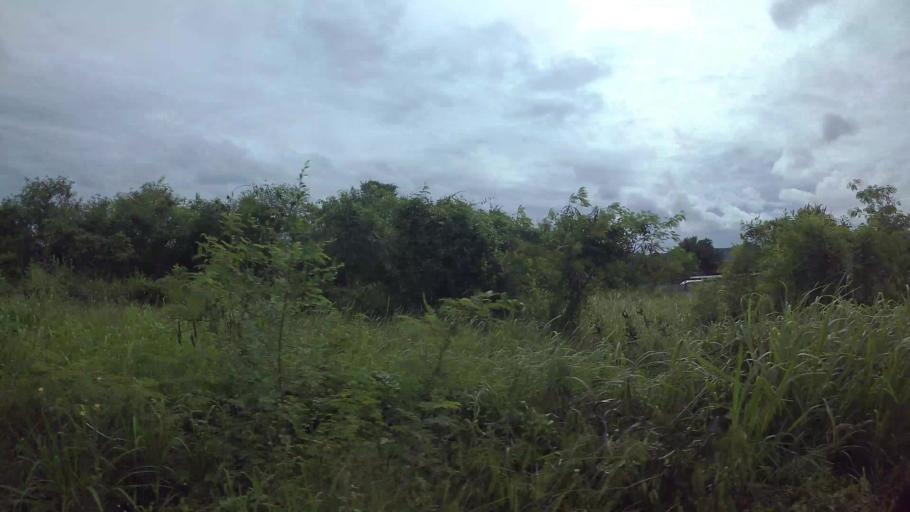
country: TH
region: Chon Buri
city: Sattahip
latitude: 12.7111
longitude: 100.9024
